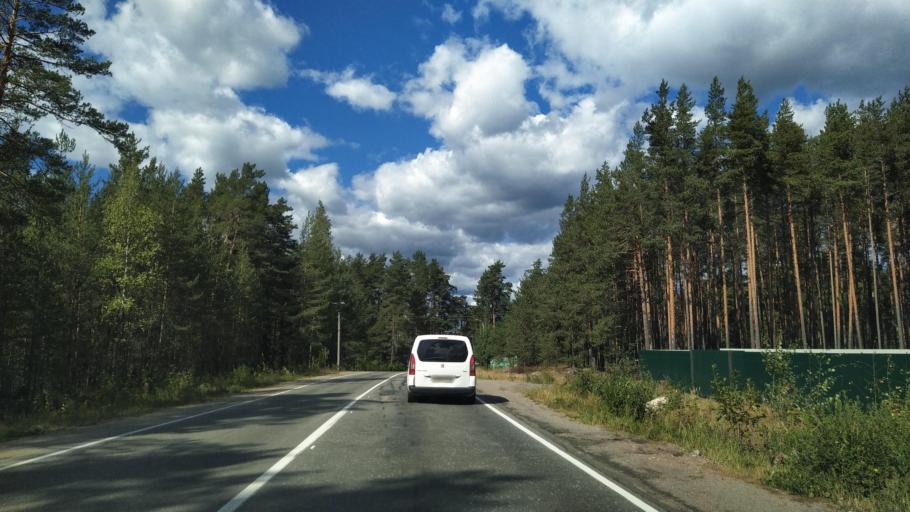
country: RU
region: Leningrad
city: Priozersk
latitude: 61.0042
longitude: 30.1845
